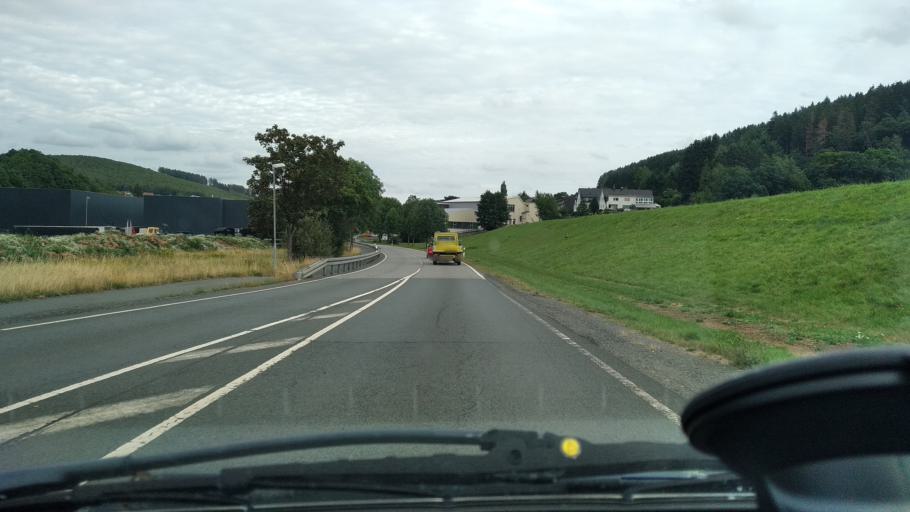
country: DE
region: Hesse
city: Dillenburg
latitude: 50.8373
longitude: 8.2971
